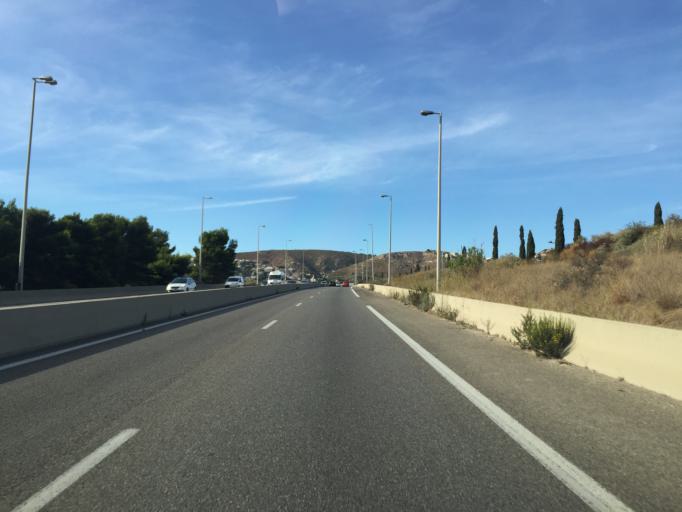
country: FR
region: Provence-Alpes-Cote d'Azur
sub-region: Departement des Bouches-du-Rhone
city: Marseille 16
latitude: 43.3581
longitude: 5.3450
